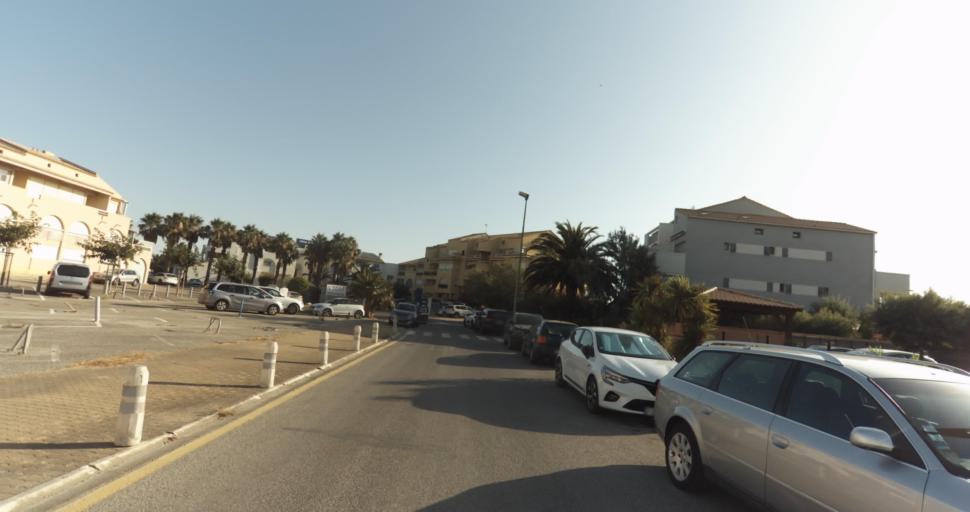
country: FR
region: Languedoc-Roussillon
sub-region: Departement des Pyrenees-Orientales
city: Saint-Cyprien-Plage
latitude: 42.6065
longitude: 3.0395
